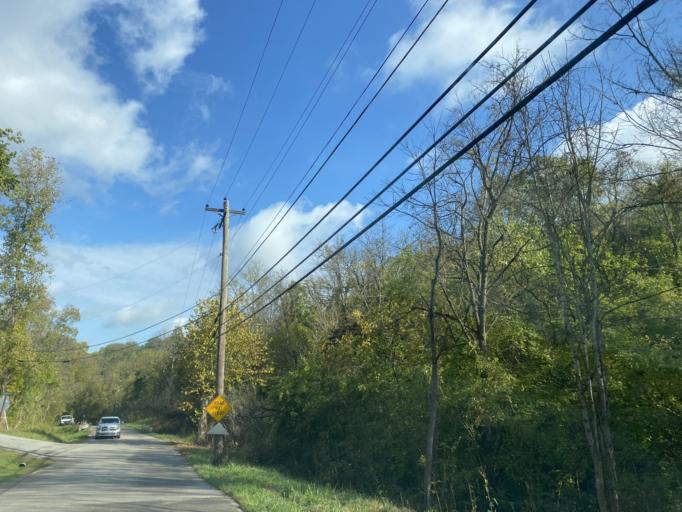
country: US
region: Kentucky
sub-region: Campbell County
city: Cold Spring
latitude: 39.0297
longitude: -84.4190
